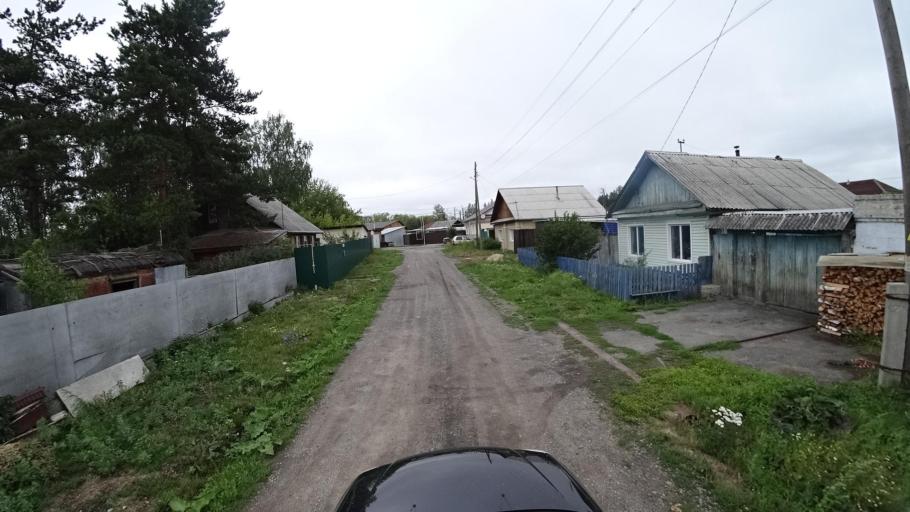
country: RU
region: Sverdlovsk
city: Kamyshlov
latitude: 56.8479
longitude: 62.7608
